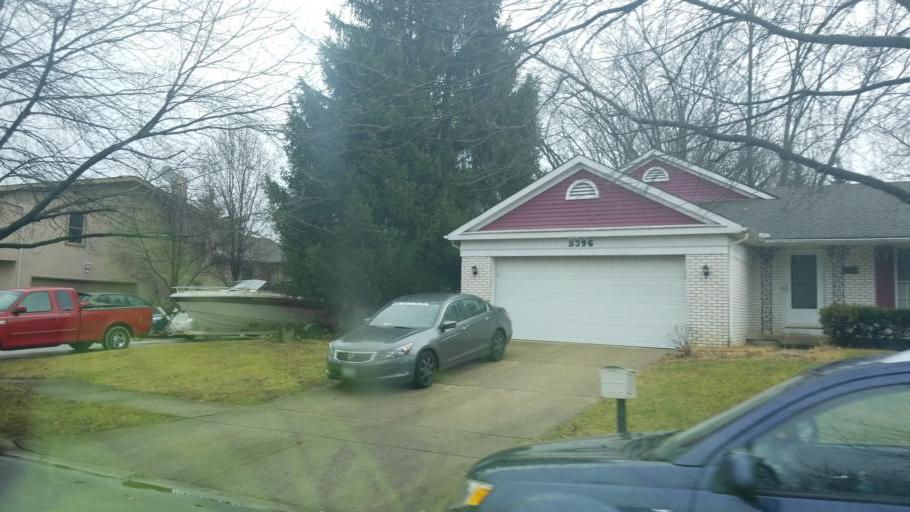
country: US
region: Ohio
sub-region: Franklin County
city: Worthington
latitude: 40.0674
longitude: -83.0647
